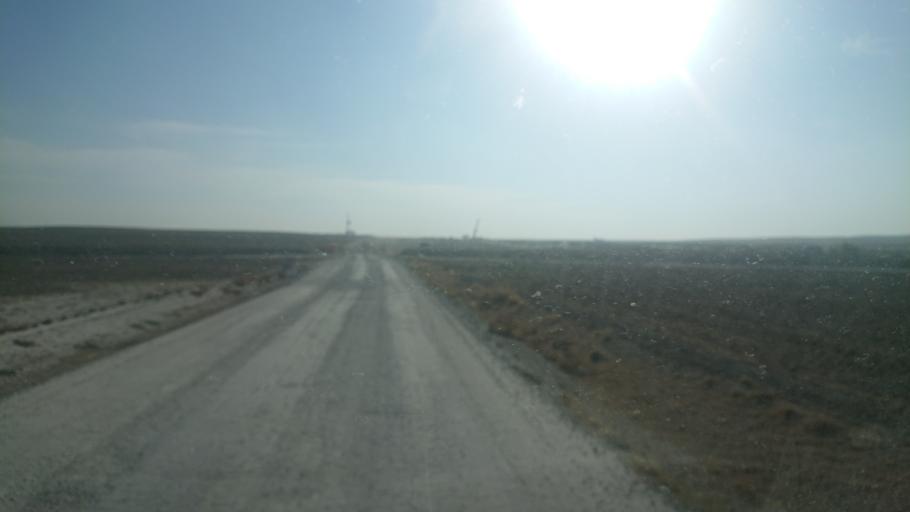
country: TR
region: Aksaray
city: Sultanhani
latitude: 38.0692
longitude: 33.6162
